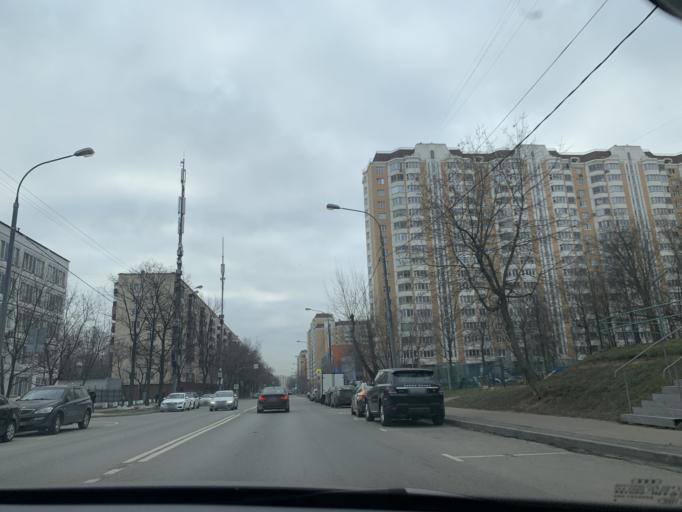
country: RU
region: Moskovskaya
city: Vostochnoe Degunino
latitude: 55.8703
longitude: 37.5609
